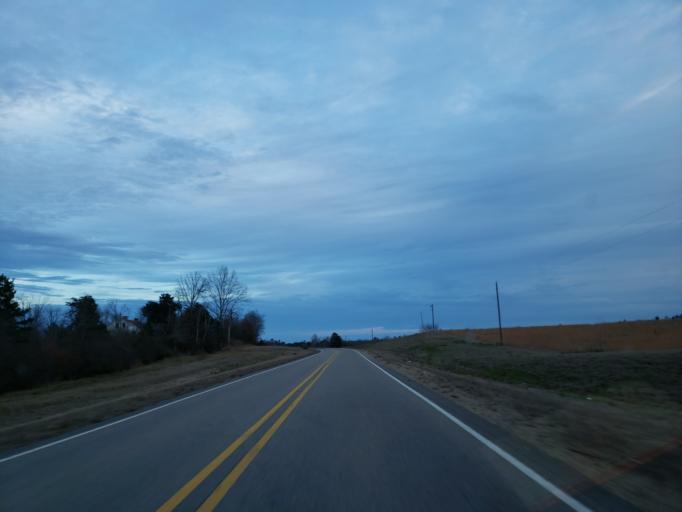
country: US
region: Mississippi
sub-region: Kemper County
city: De Kalb
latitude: 32.8308
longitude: -88.3866
